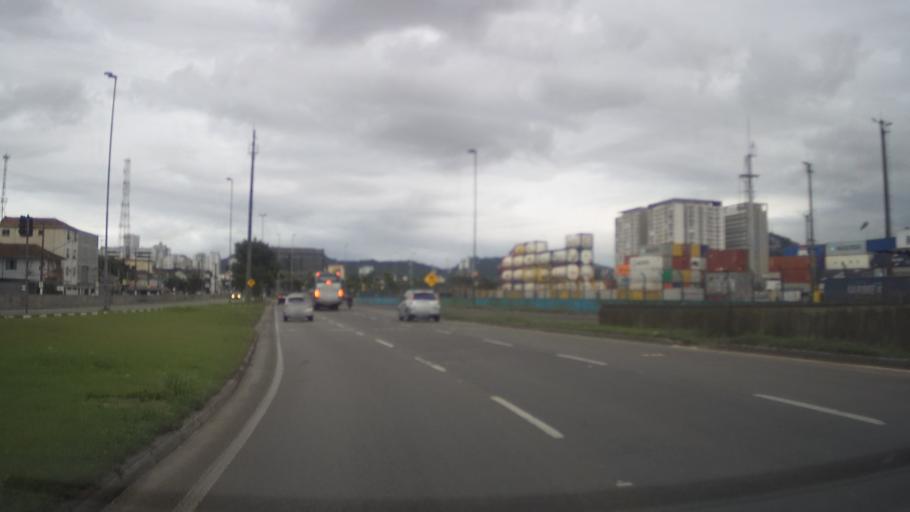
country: BR
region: Sao Paulo
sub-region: Santos
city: Santos
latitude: -23.9505
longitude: -46.3149
